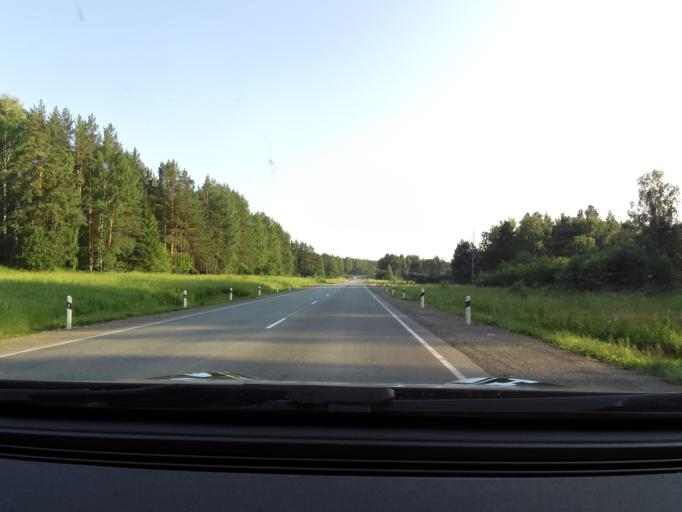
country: RU
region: Sverdlovsk
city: Nizhniye Sergi
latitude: 56.5951
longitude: 59.2283
